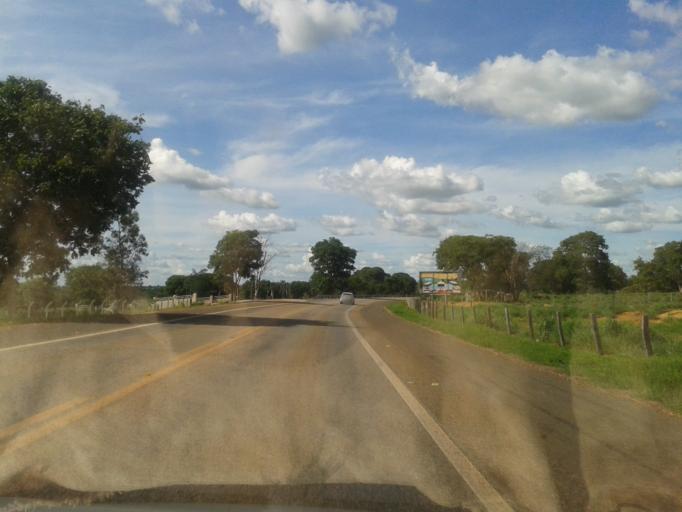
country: BR
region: Goias
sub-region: Mozarlandia
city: Mozarlandia
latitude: -15.0843
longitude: -50.6231
